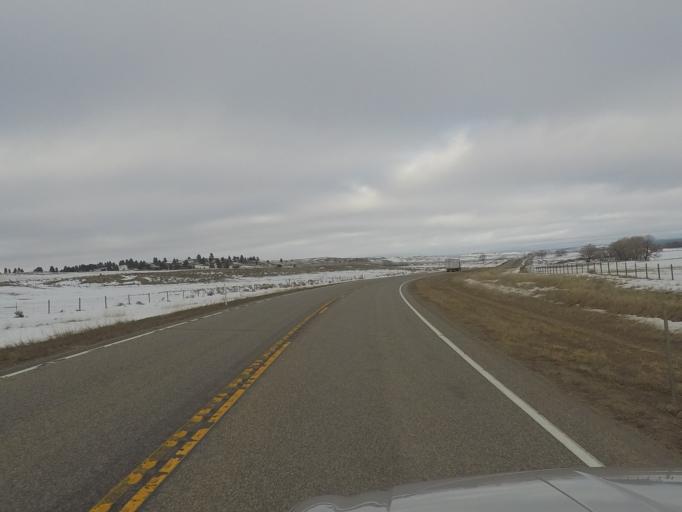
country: US
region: Montana
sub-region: Golden Valley County
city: Ryegate
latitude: 46.3061
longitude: -109.0119
